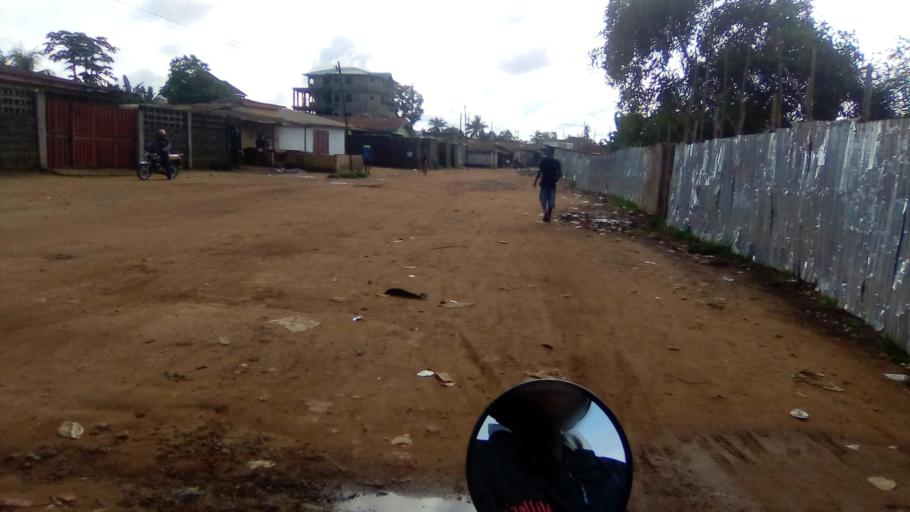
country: SL
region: Southern Province
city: Bo
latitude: 7.9563
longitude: -11.7560
